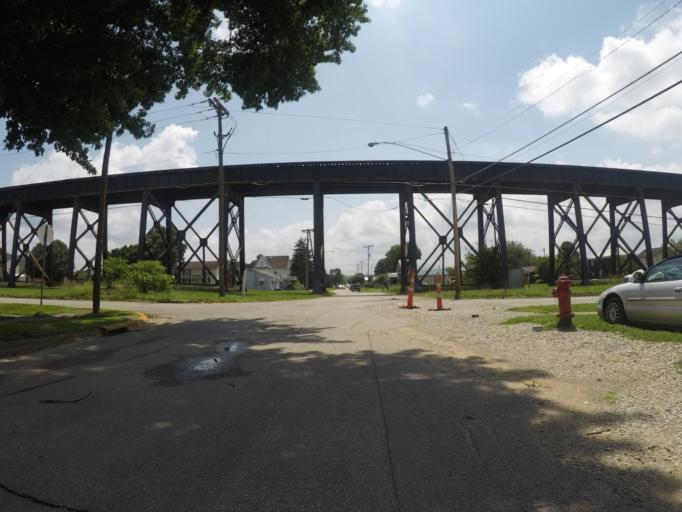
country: US
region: West Virginia
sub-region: Wayne County
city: Kenova
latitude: 38.4016
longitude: -82.5757
